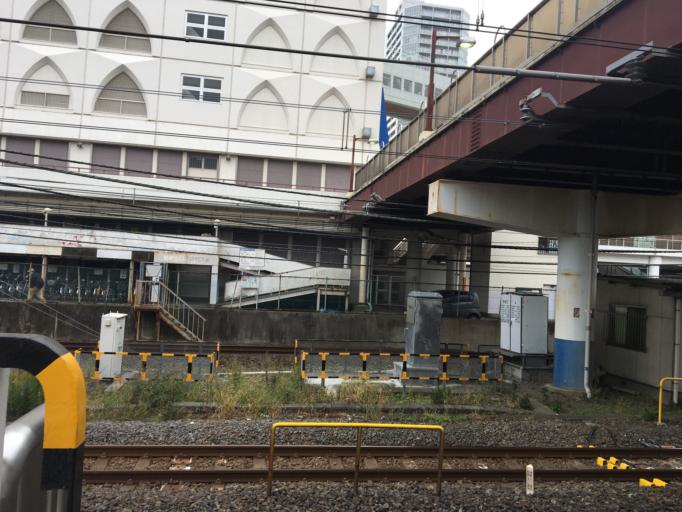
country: JP
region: Chiba
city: Kashiwa
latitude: 35.8632
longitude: 139.9720
